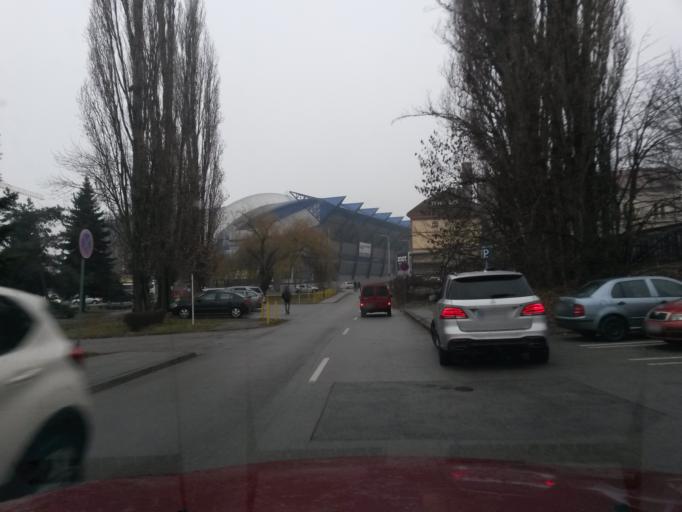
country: SK
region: Kosicky
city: Kosice
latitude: 48.7168
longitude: 21.2473
